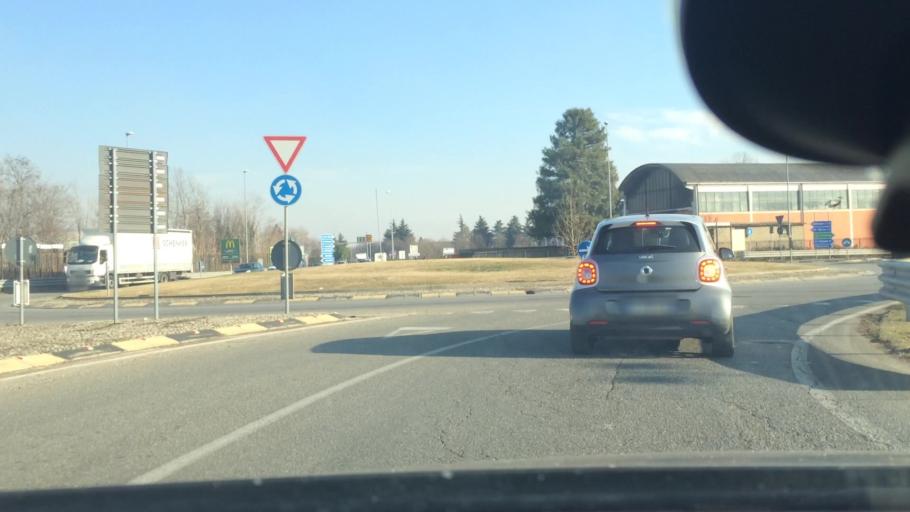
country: IT
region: Lombardy
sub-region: Citta metropolitana di Milano
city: Arluno
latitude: 45.4986
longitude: 8.9349
